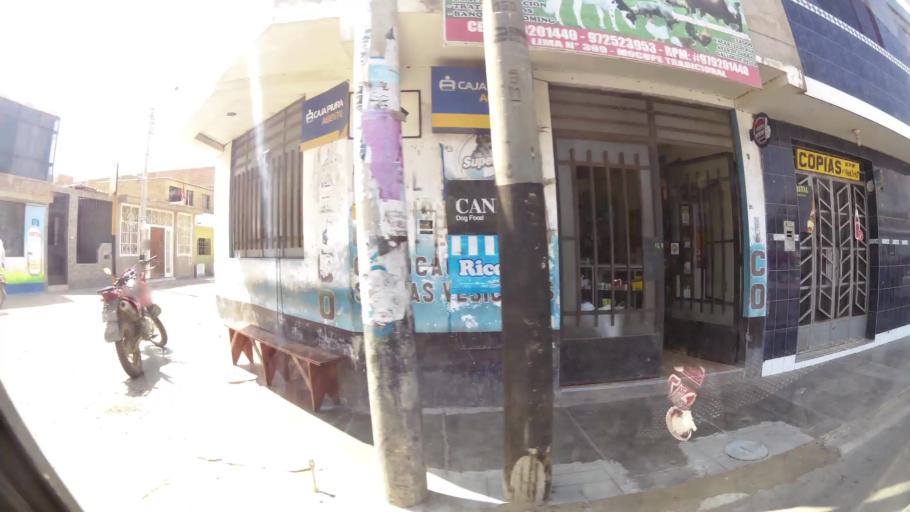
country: PE
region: Lambayeque
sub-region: Provincia de Chiclayo
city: Mocupe
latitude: -6.9907
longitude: -79.6225
